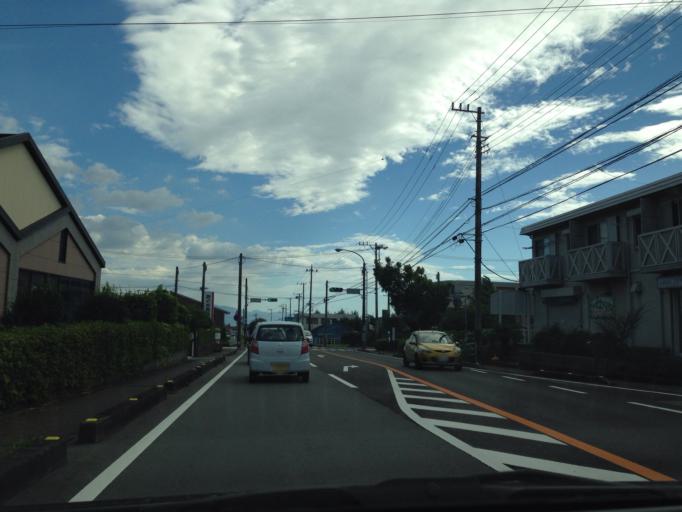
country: JP
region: Shizuoka
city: Mishima
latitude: 35.1986
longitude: 138.9148
